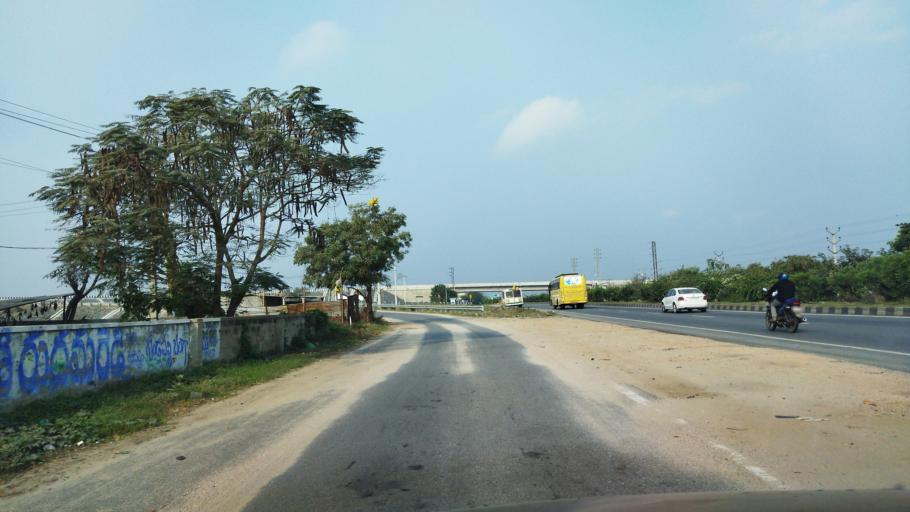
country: IN
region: Telangana
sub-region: Nalgonda
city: Nalgonda
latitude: 17.1682
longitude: 79.3979
